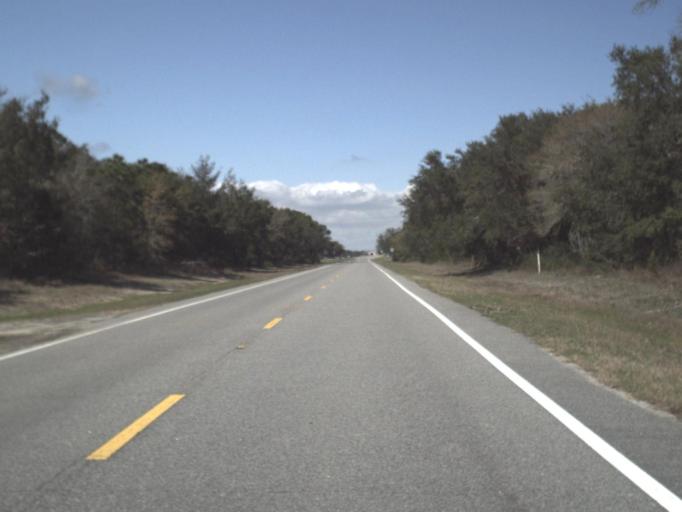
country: US
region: Florida
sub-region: Wakulla County
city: Crawfordville
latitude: 29.9547
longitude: -84.3853
